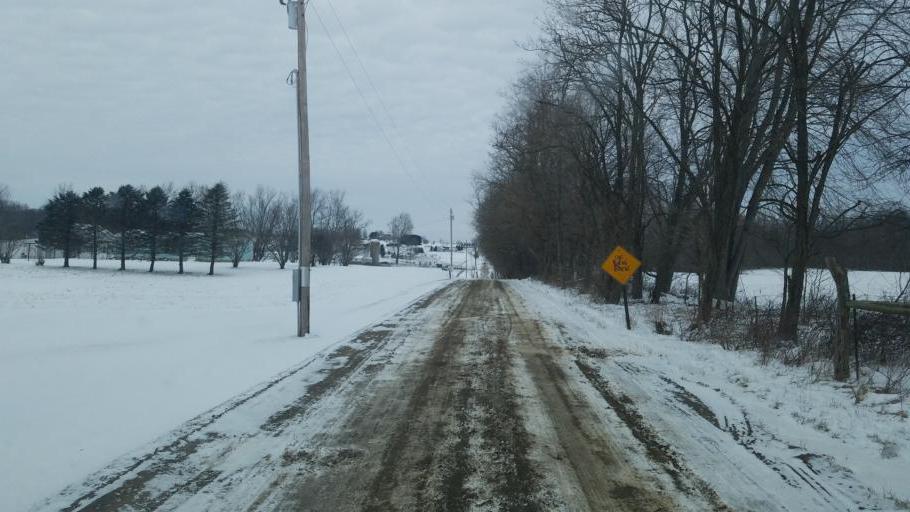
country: US
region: Ohio
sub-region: Knox County
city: Fredericktown
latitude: 40.5100
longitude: -82.6147
